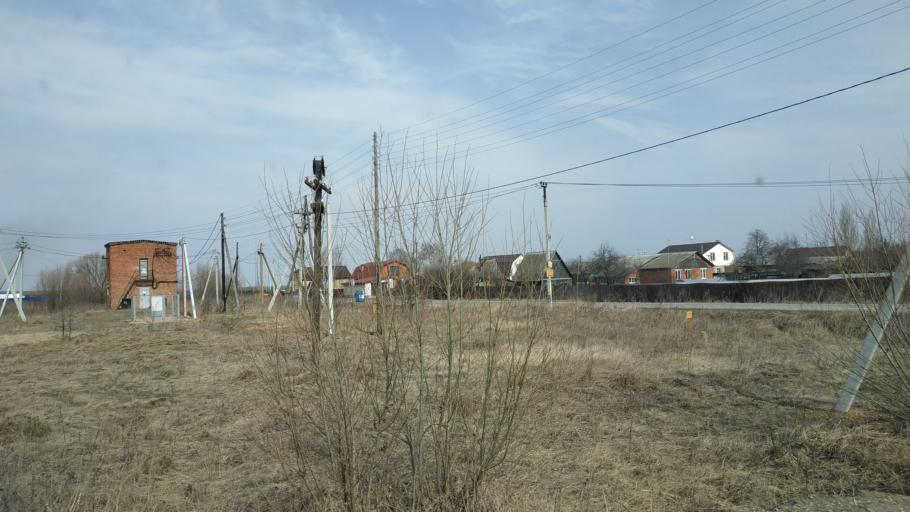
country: RU
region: Moskovskaya
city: Troitskoye
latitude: 55.3601
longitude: 38.5453
